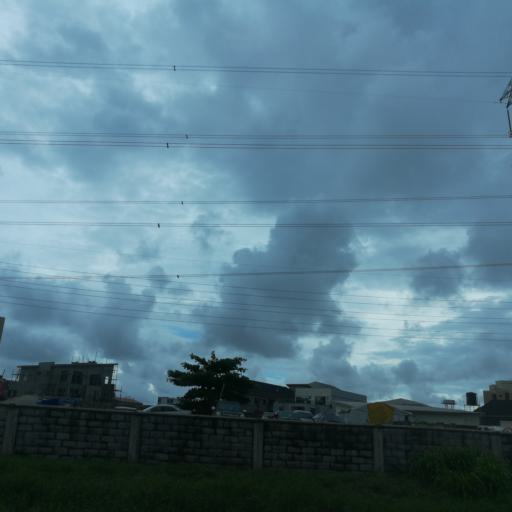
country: NG
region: Lagos
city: Ikoyi
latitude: 6.4322
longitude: 3.4588
